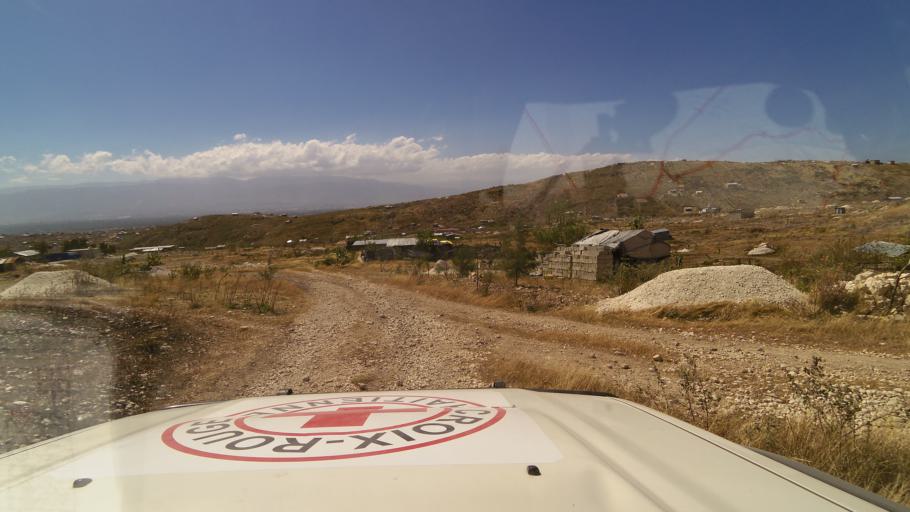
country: HT
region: Ouest
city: Croix des Bouquets
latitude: 18.6766
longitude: -72.2863
